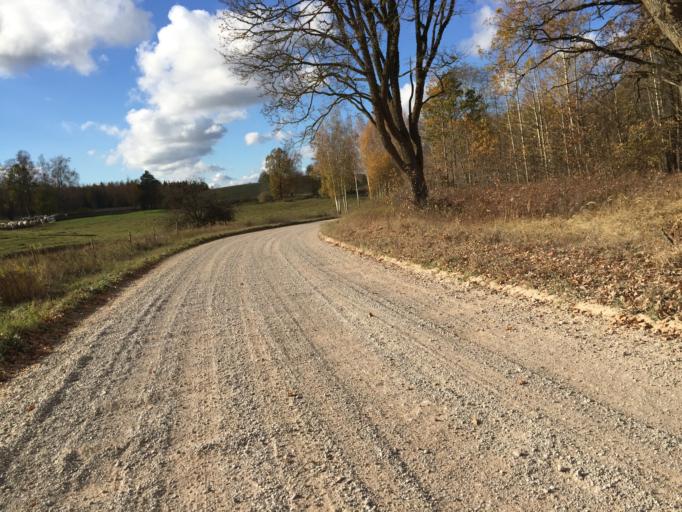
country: LV
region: Tukuma Rajons
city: Tukums
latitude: 56.9599
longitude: 22.9831
